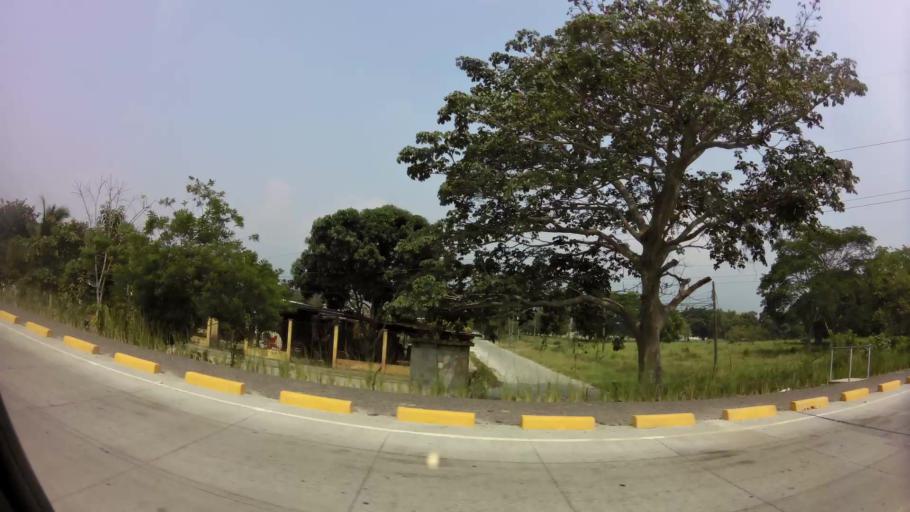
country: HN
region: Cortes
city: San Pedro Sula
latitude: 15.5440
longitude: -87.9986
